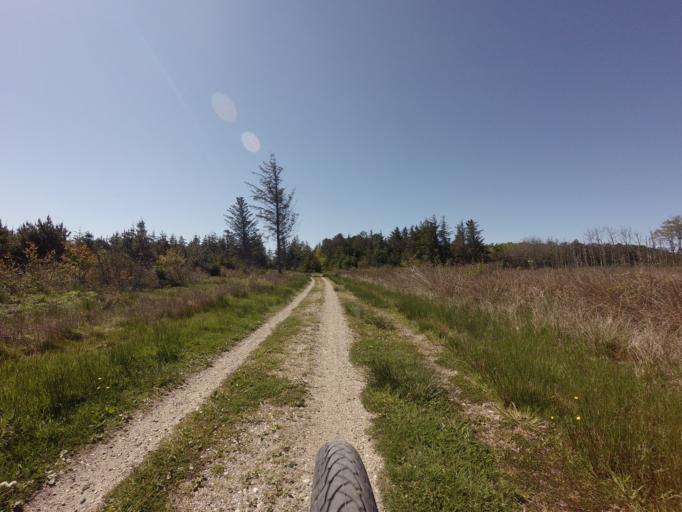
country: DK
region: North Denmark
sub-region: Jammerbugt Kommune
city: Pandrup
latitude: 57.2838
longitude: 9.6363
